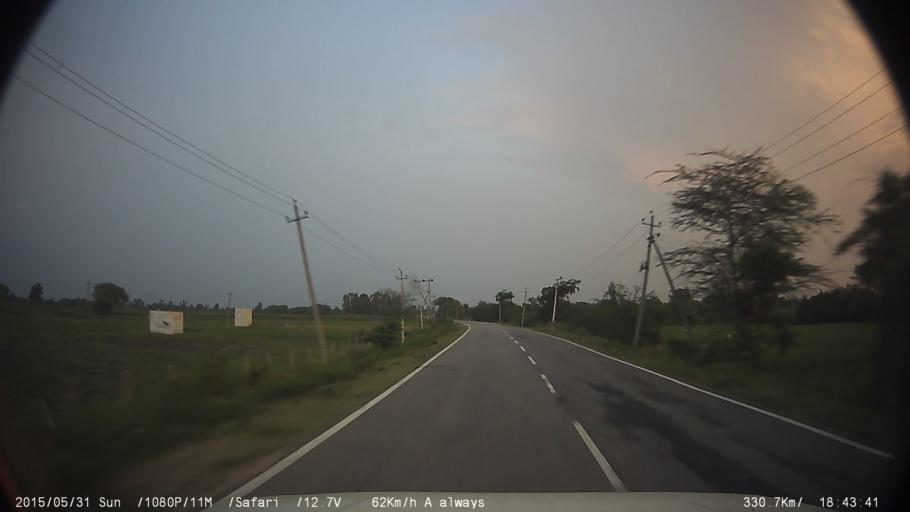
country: IN
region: Karnataka
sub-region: Mysore
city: Tirumakudal Narsipur
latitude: 12.1567
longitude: 76.8085
